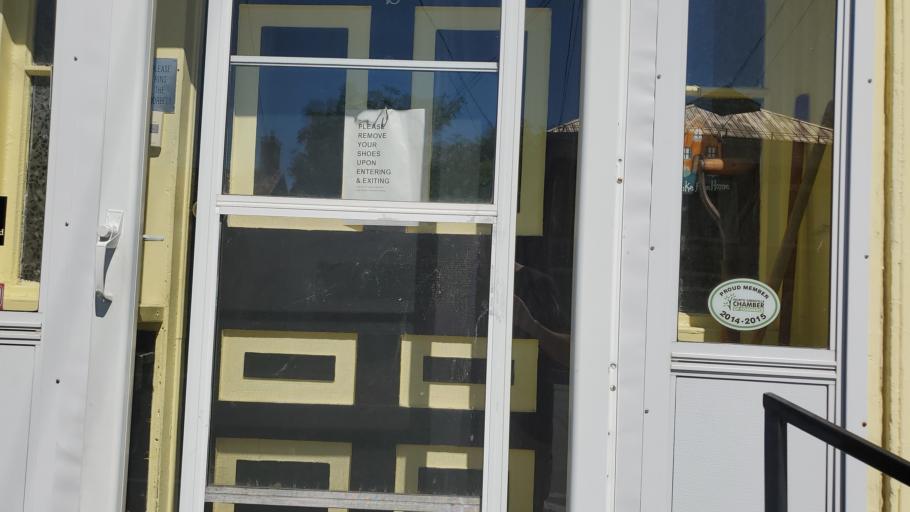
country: CA
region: Ontario
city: Prescott
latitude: 45.0163
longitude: -75.6479
